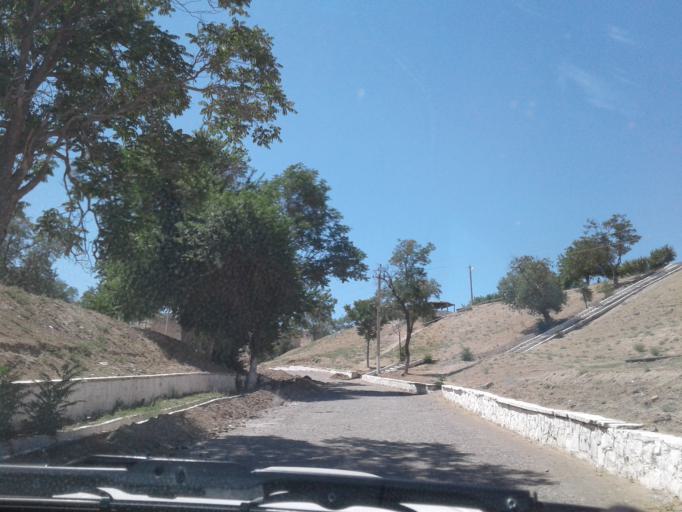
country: TM
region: Mary
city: Serhetabat
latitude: 35.2774
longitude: 62.3436
